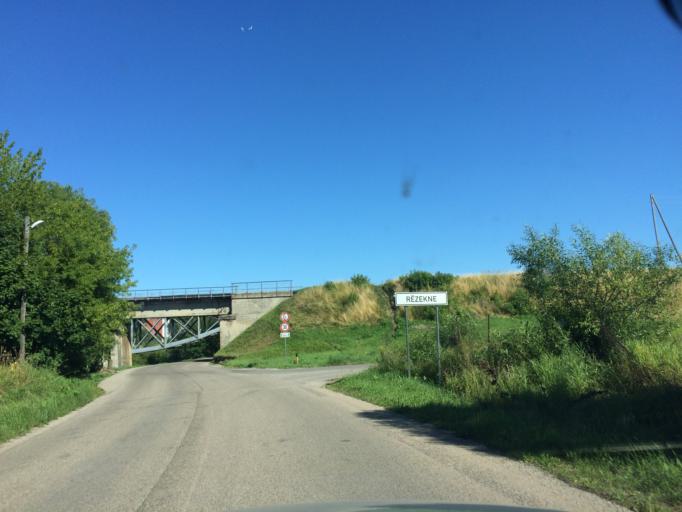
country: LV
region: Rezekne
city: Rezekne
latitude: 56.5076
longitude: 27.3164
